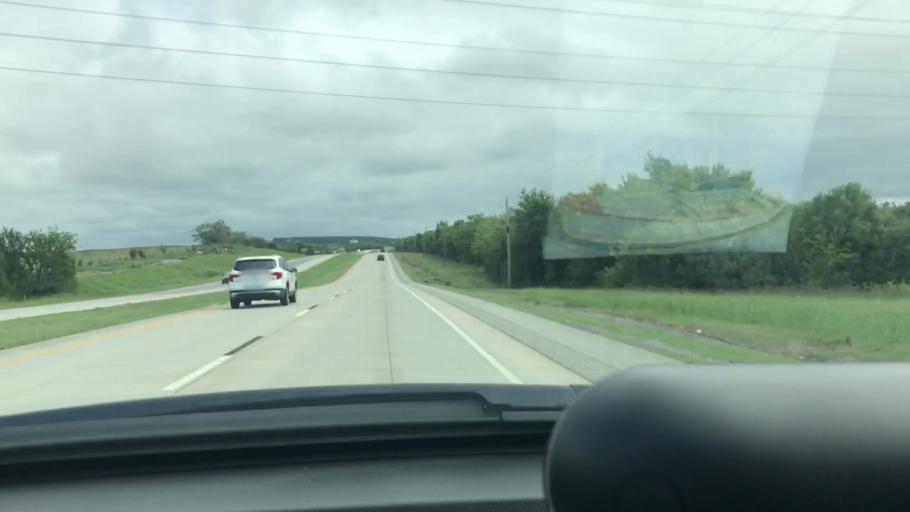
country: US
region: Oklahoma
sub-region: Atoka County
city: Atoka
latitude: 34.4097
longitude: -96.1075
